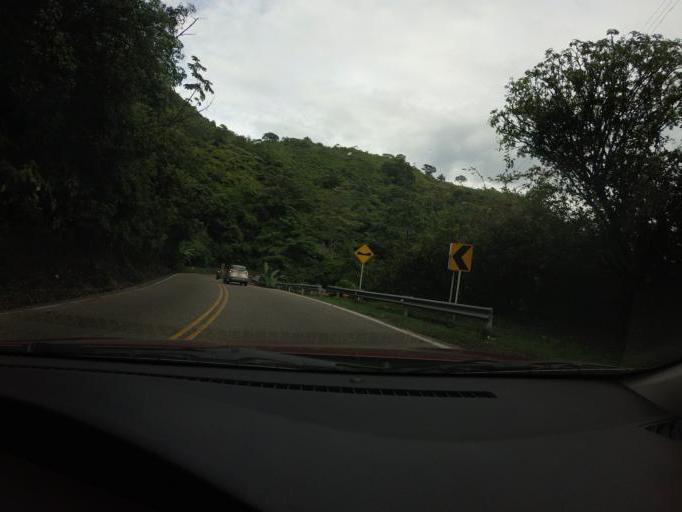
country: CO
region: Cundinamarca
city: Villeta
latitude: 5.0231
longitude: -74.5229
